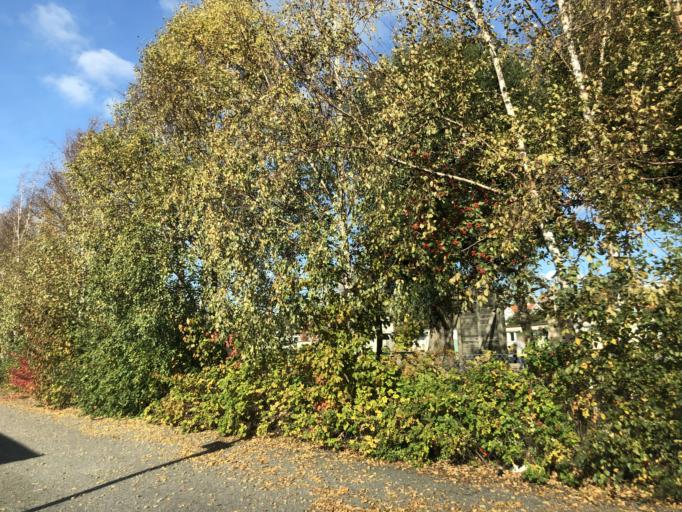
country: SE
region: Vaestra Goetaland
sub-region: Goteborg
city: Billdal
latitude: 57.6300
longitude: 11.9386
